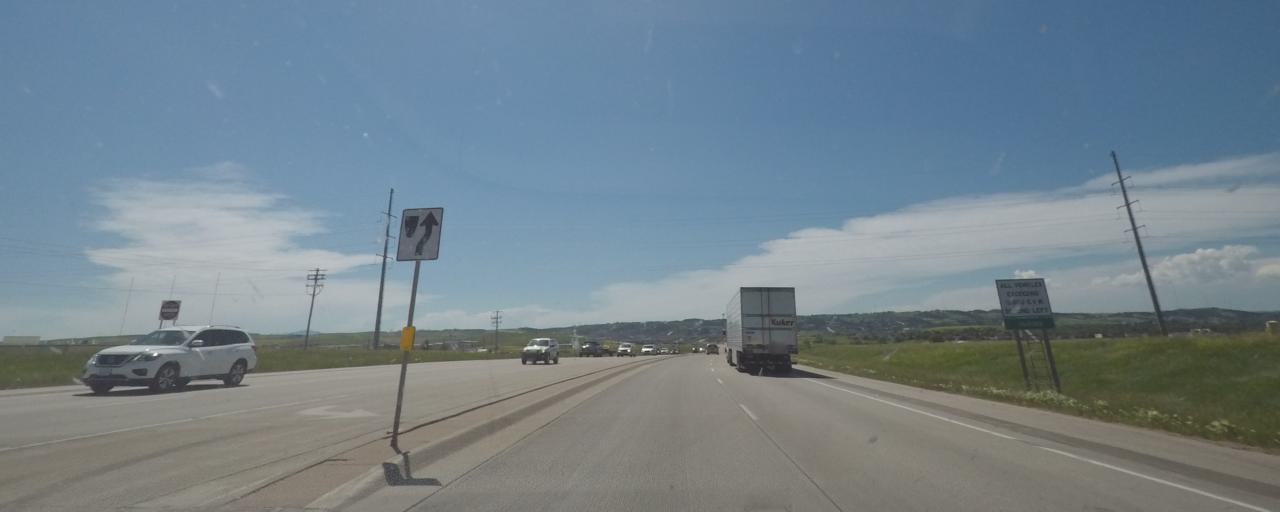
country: US
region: South Dakota
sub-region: Pennington County
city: Rapid Valley
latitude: 44.0390
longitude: -103.1797
